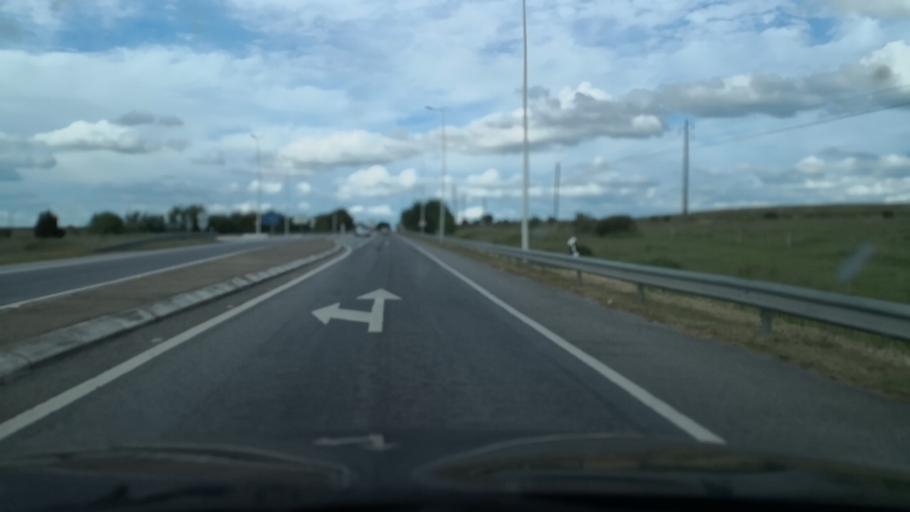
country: PT
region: Evora
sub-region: Evora
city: Evora
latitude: 38.6405
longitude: -7.8527
